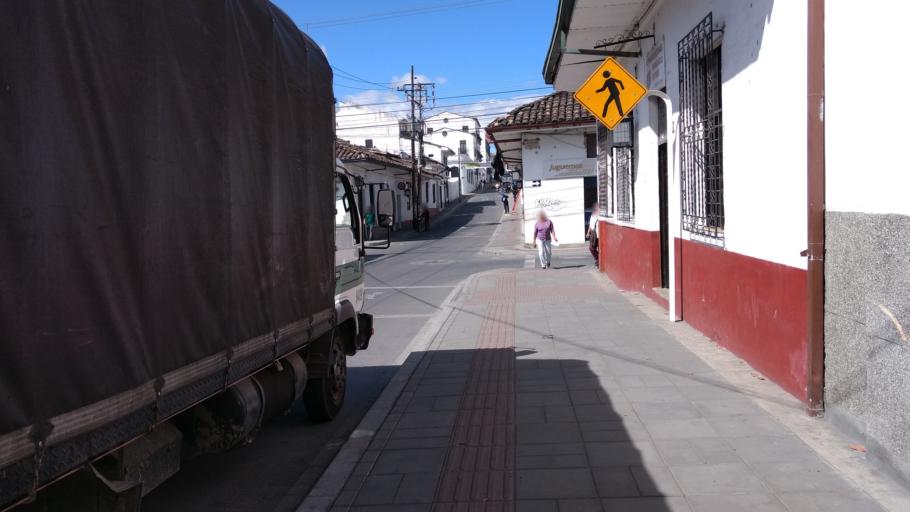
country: CO
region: Cauca
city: Popayan
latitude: 2.4449
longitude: -76.6077
